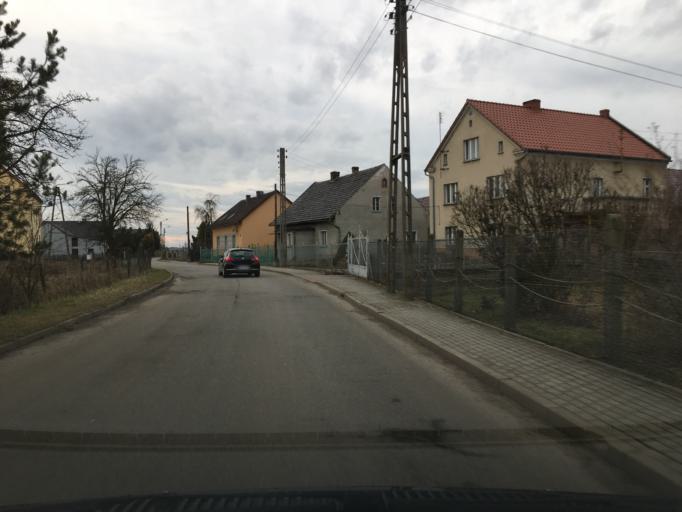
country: PL
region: Opole Voivodeship
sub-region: Powiat kedzierzynsko-kozielski
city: Wiekszyce
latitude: 50.3562
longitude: 18.1217
